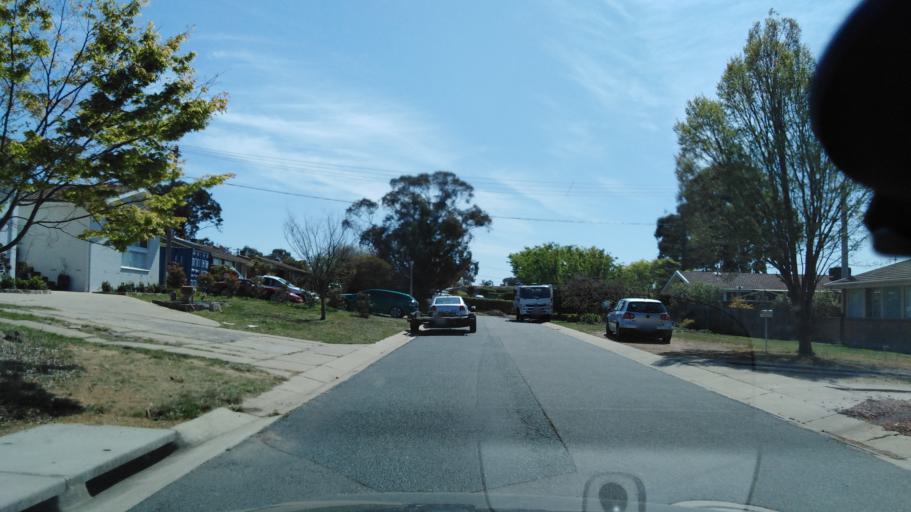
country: AU
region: Australian Capital Territory
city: Macquarie
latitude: -35.3458
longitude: 149.0298
